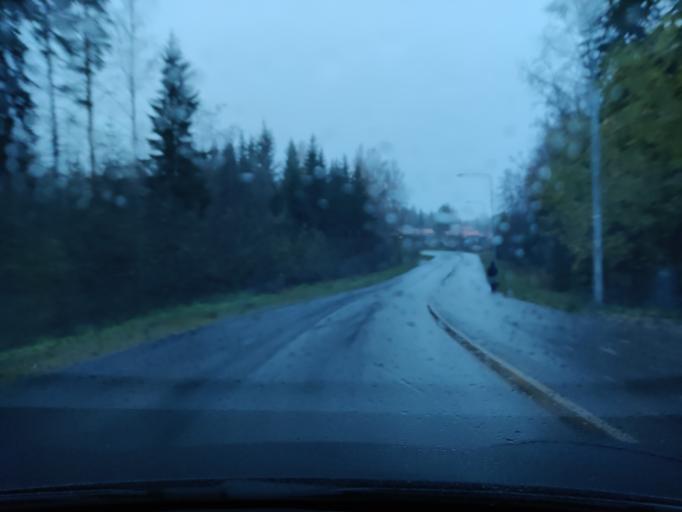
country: FI
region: Northern Savo
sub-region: Kuopio
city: Kuopio
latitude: 62.8301
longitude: 27.7160
